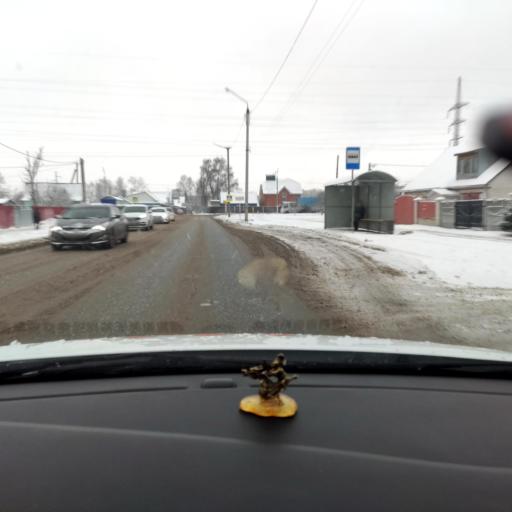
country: RU
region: Tatarstan
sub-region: Zelenodol'skiy Rayon
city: Zelenodolsk
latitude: 55.8525
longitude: 48.5302
